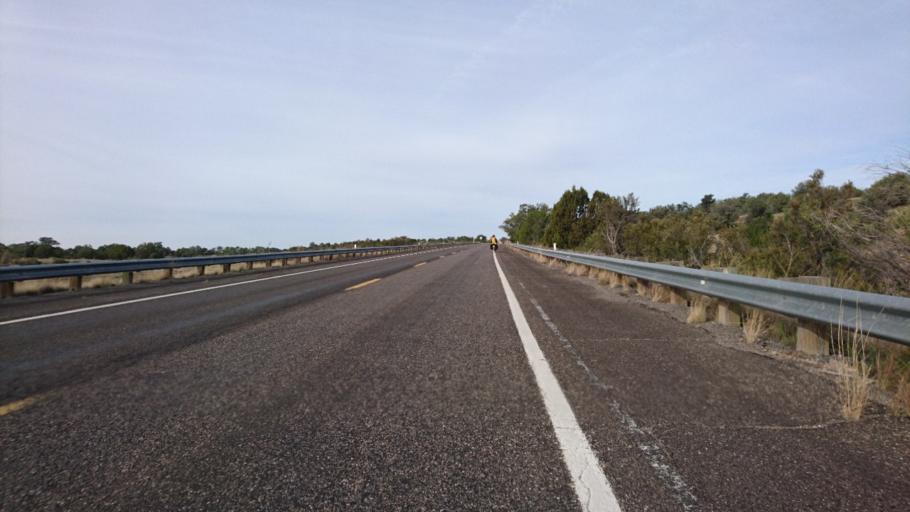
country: US
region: Arizona
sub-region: Mohave County
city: Peach Springs
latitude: 35.5522
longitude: -113.3544
